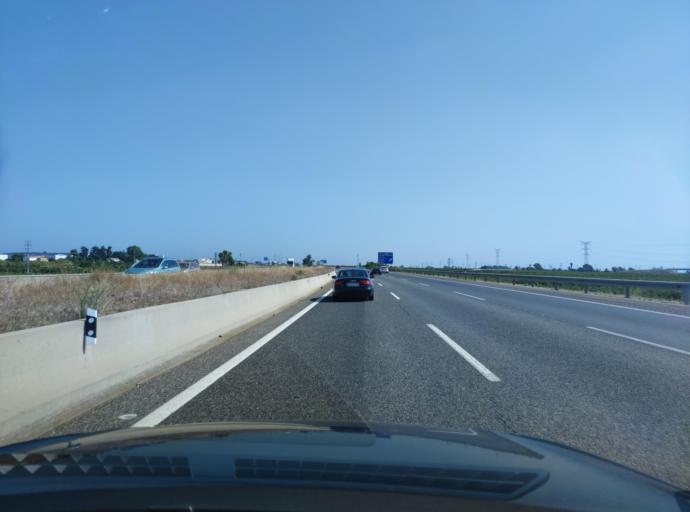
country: ES
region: Valencia
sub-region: Provincia de Valencia
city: Alginet
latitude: 39.2634
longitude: -0.4589
